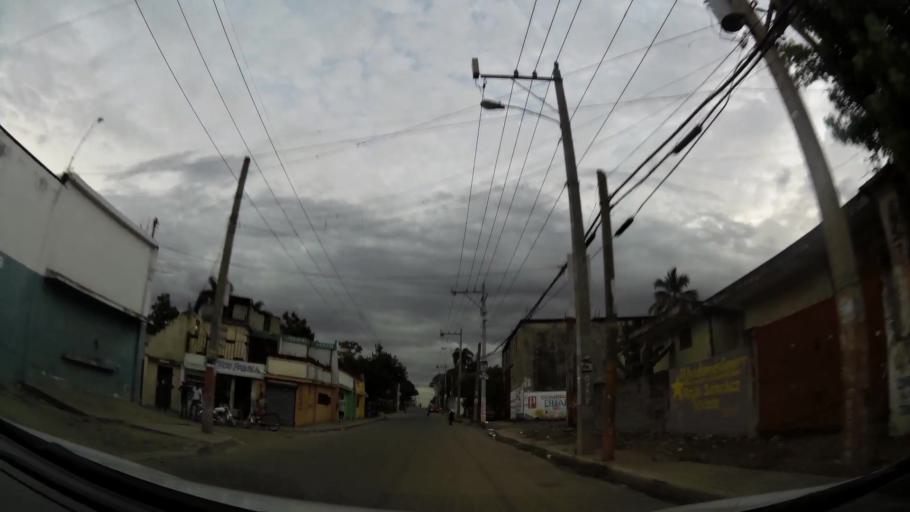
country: DO
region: Santo Domingo
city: Santo Domingo Oeste
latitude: 18.5209
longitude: -70.0339
